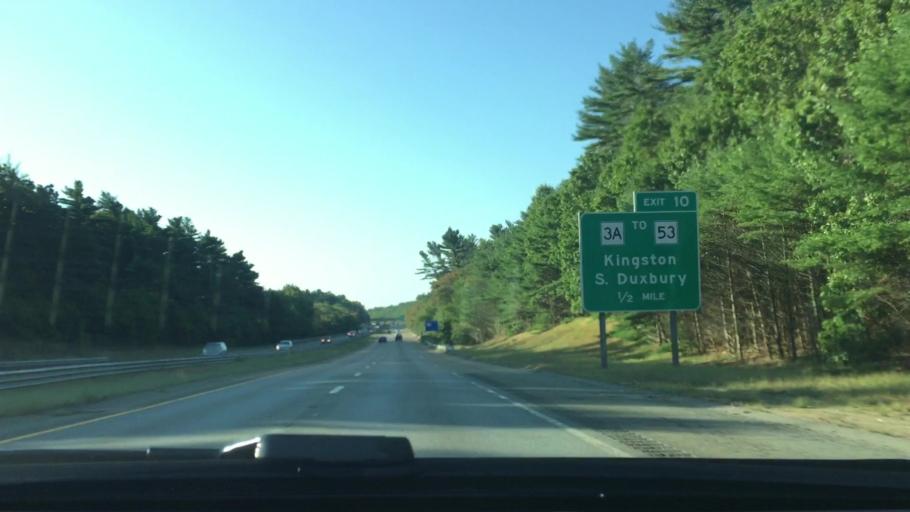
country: US
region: Massachusetts
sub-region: Plymouth County
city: Kingston
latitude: 42.0244
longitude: -70.7260
